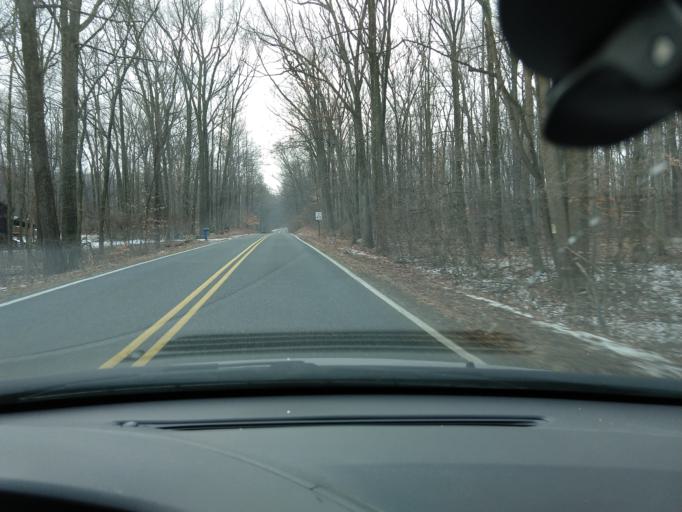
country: US
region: Pennsylvania
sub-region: Berks County
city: Birdsboro
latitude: 40.2365
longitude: -75.7722
